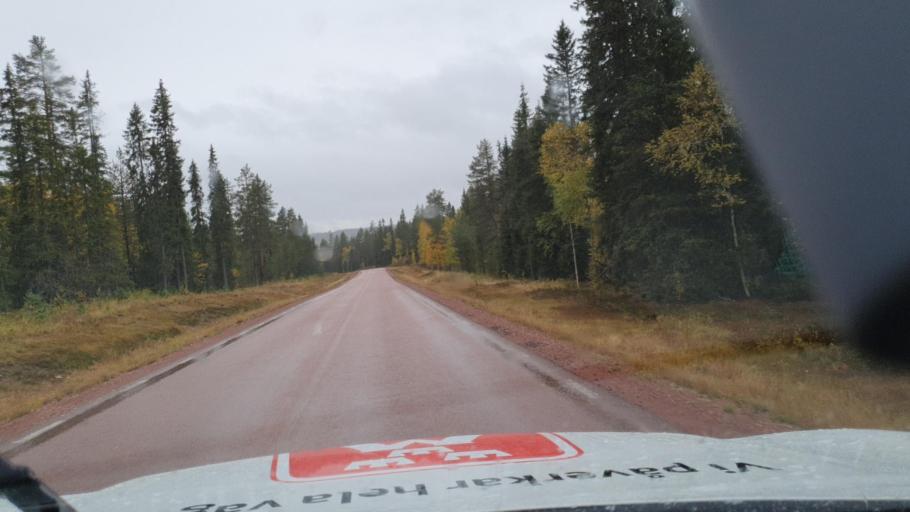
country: SE
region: Dalarna
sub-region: Alvdalens Kommun
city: AElvdalen
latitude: 61.4498
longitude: 14.1499
